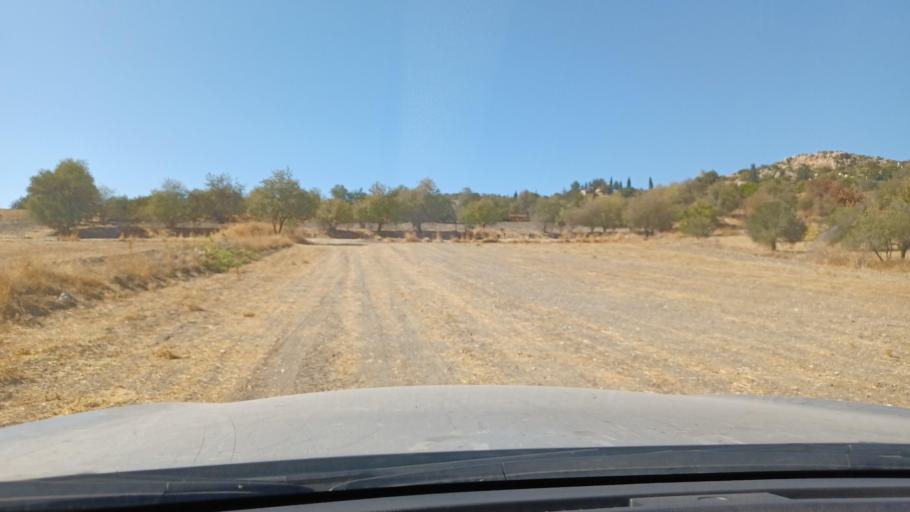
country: CY
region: Pafos
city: Polis
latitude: 34.9702
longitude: 32.5085
